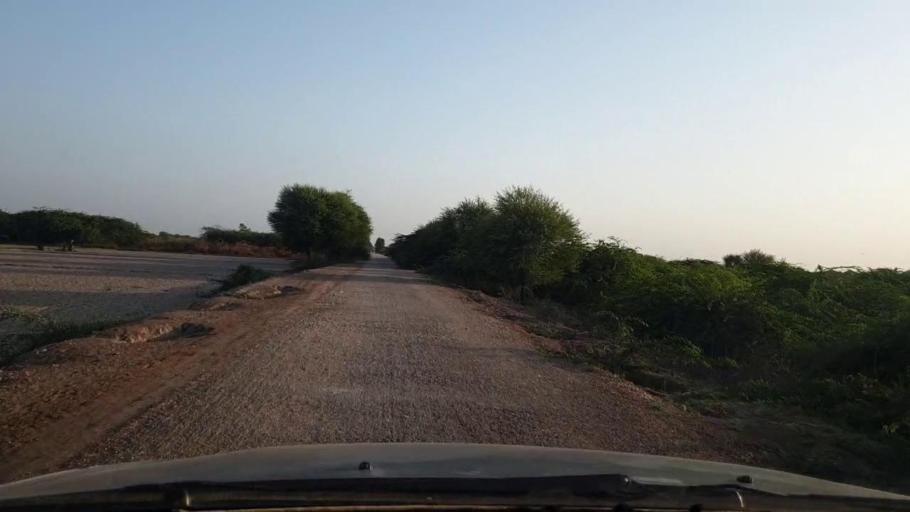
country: PK
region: Sindh
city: Tando Ghulam Ali
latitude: 25.1105
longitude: 68.9387
